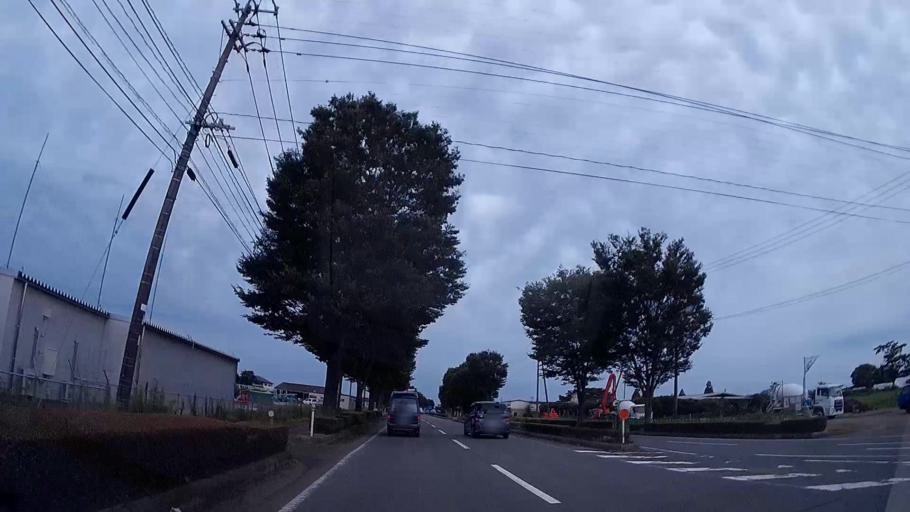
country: JP
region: Kumamoto
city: Ozu
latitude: 32.9082
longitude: 130.8474
